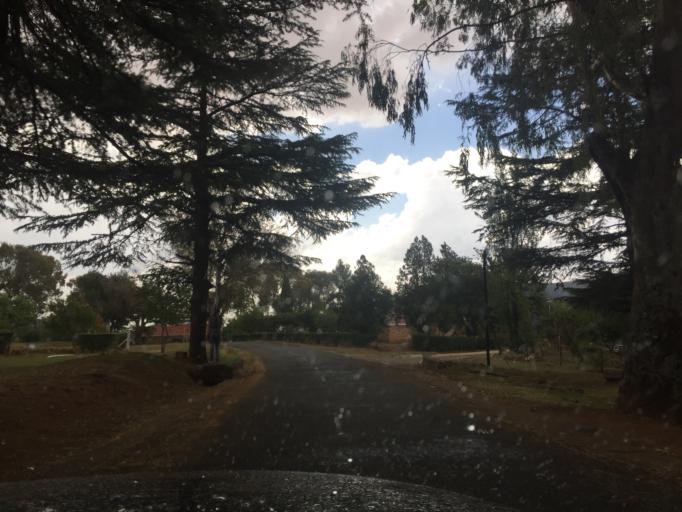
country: LS
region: Maseru
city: Nako
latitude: -29.4479
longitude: 27.7218
